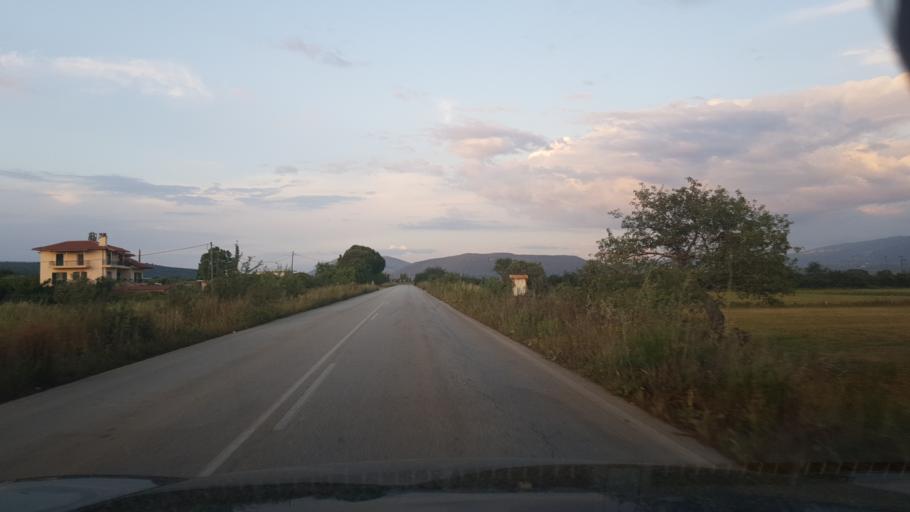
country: GR
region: West Greece
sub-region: Nomos Aitolias kai Akarnanias
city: Vonitsa
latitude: 38.8714
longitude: 20.8093
